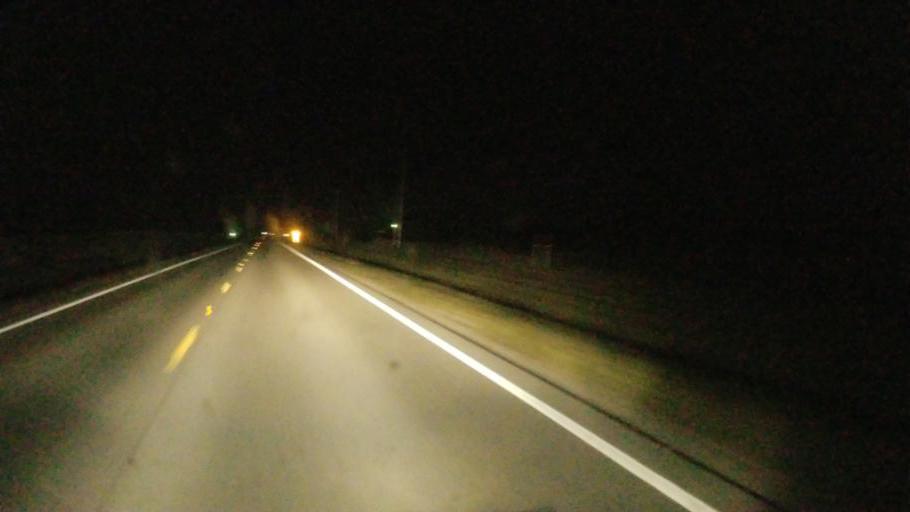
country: US
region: Ohio
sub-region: Hardin County
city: Kenton
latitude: 40.5603
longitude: -83.5425
